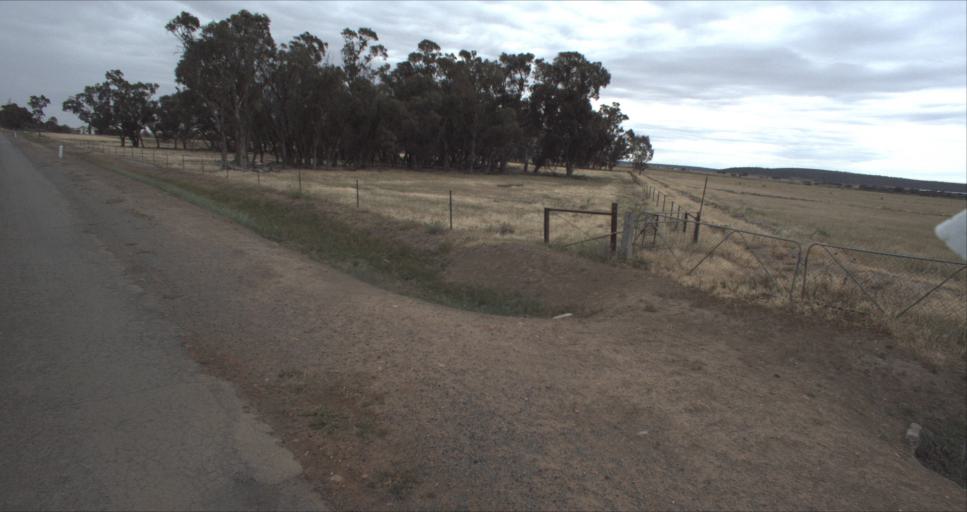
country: AU
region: New South Wales
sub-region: Leeton
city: Leeton
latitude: -34.4099
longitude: 146.3405
